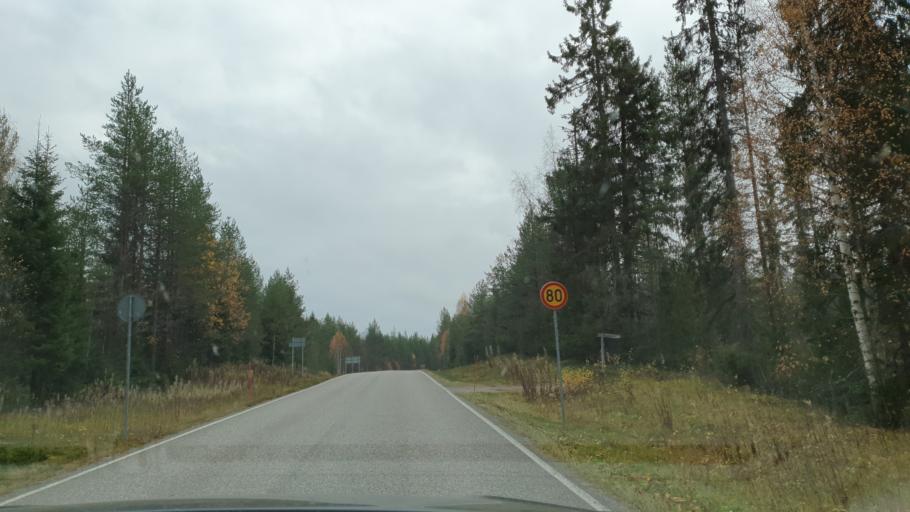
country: FI
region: Kainuu
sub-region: Kajaani
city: Paltamo
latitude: 64.6503
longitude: 27.9630
